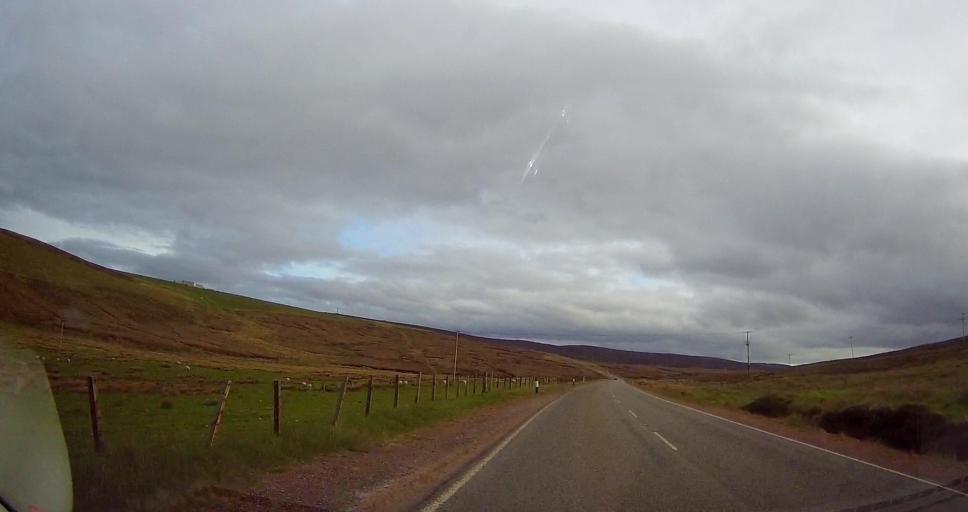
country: GB
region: Scotland
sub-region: Shetland Islands
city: Lerwick
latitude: 60.4589
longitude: -1.2103
